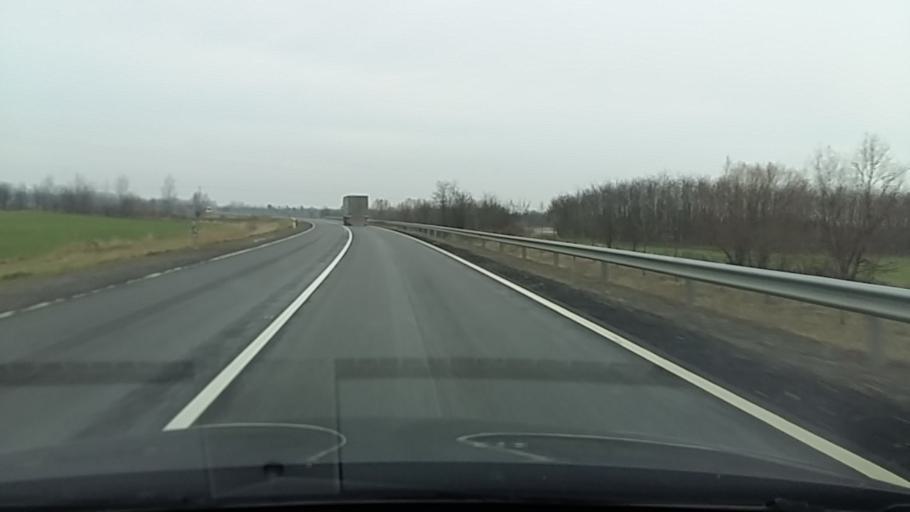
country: HU
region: Szabolcs-Szatmar-Bereg
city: Nyirpazony
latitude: 47.9620
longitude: 21.8157
